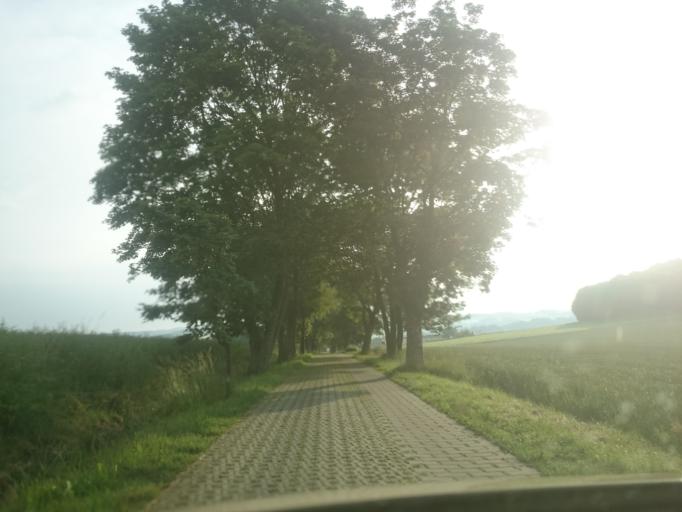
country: DE
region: Saxony
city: Bornichen
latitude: 50.7601
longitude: 13.1488
